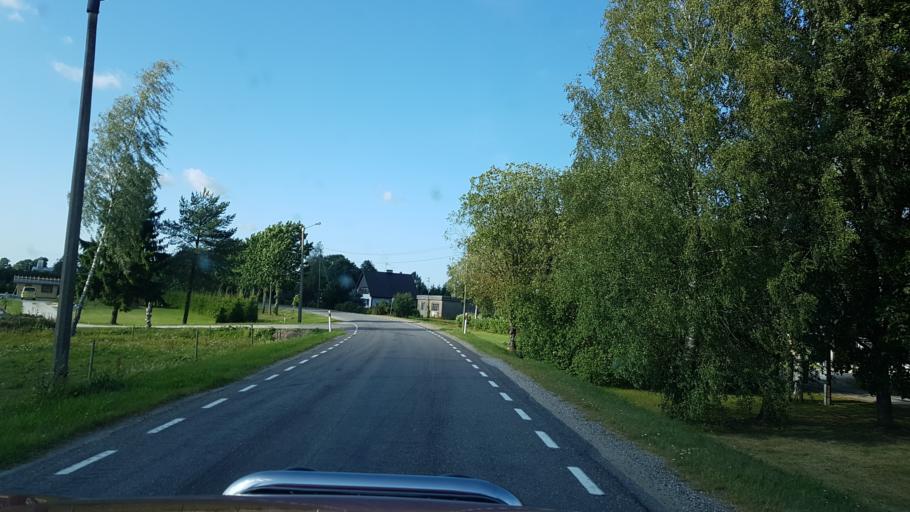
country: EE
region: Jaervamaa
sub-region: Jaerva-Jaani vald
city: Jarva-Jaani
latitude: 59.0917
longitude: 25.6822
